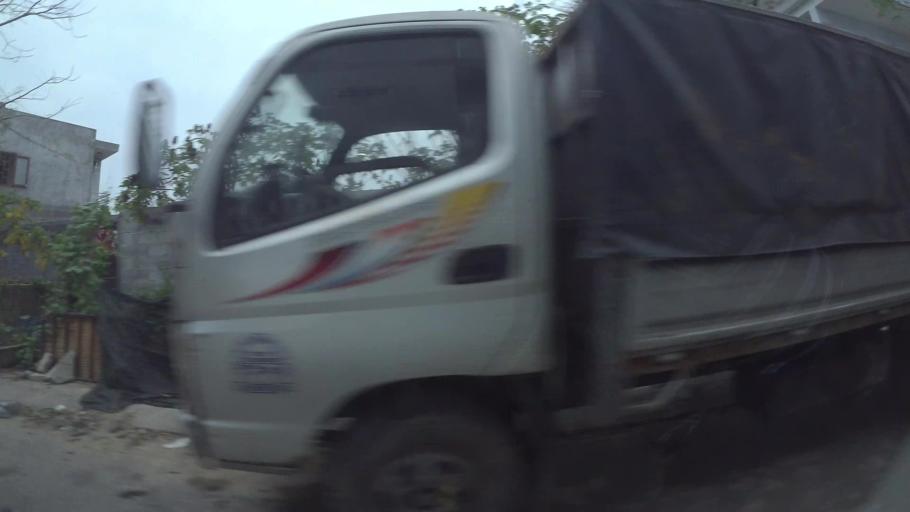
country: VN
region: Da Nang
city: Thanh Khe
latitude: 16.0474
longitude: 108.1785
